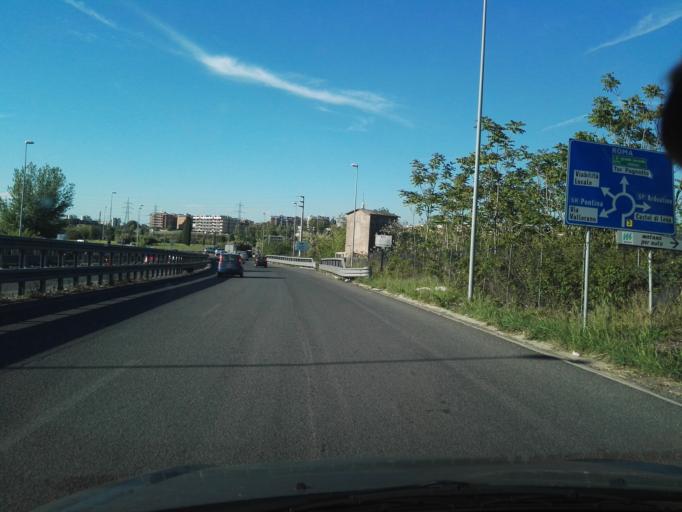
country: IT
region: Latium
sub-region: Citta metropolitana di Roma Capitale
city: Selcetta
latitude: 41.7865
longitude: 12.4821
